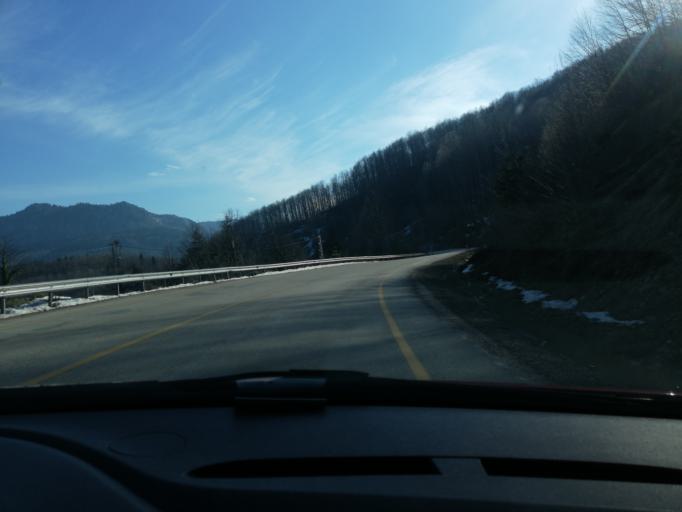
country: TR
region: Kastamonu
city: Senpazar
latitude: 41.8057
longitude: 33.1164
